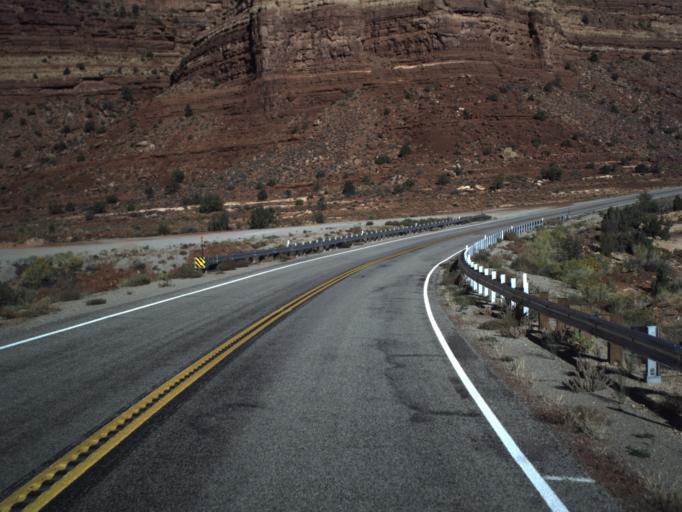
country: US
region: Utah
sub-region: San Juan County
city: Blanding
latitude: 37.7423
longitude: -110.2799
